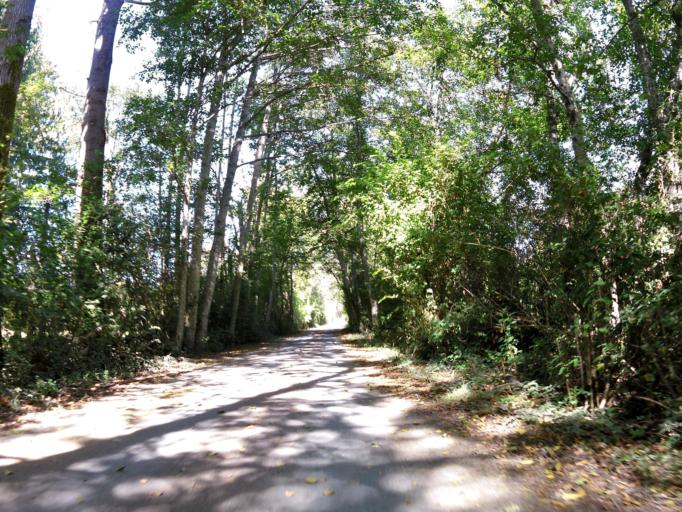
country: CA
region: British Columbia
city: Victoria
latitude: 48.5493
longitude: -123.3855
